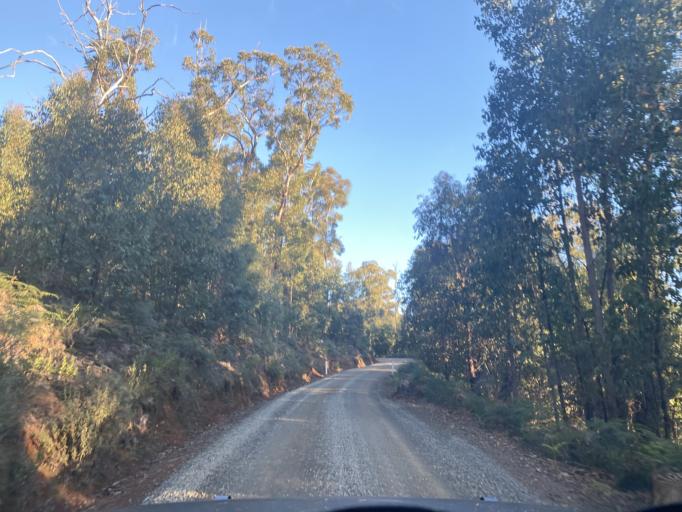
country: AU
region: Victoria
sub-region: Yarra Ranges
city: Healesville
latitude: -37.4202
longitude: 145.5297
